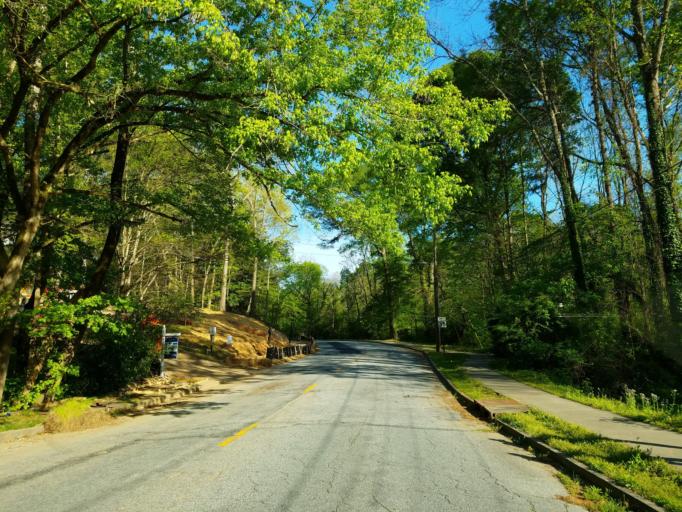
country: US
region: Georgia
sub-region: Cobb County
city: Vinings
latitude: 33.8252
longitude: -84.4150
